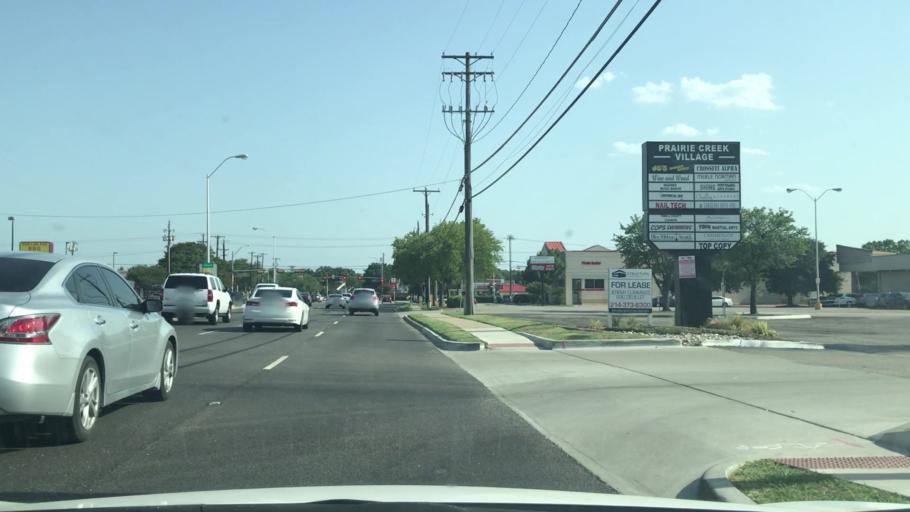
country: US
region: Texas
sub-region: Collin County
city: Plano
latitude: 33.0210
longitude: -96.7500
